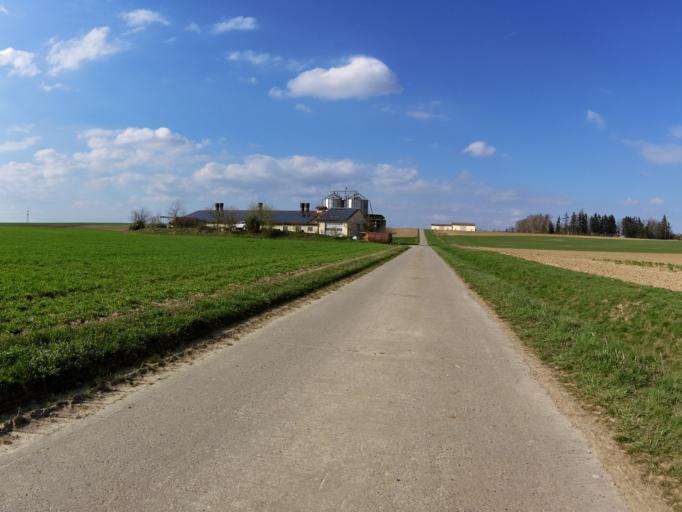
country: DE
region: Bavaria
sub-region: Regierungsbezirk Unterfranken
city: Biebelried
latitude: 49.7910
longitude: 10.0805
